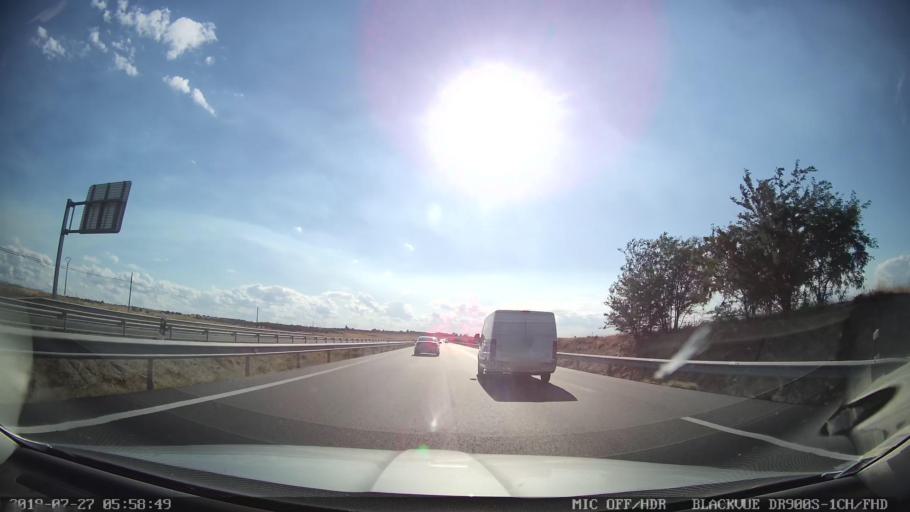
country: ES
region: Castille-La Mancha
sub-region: Province of Toledo
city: Herreruela de Oropesa
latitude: 39.9024
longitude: -5.2554
